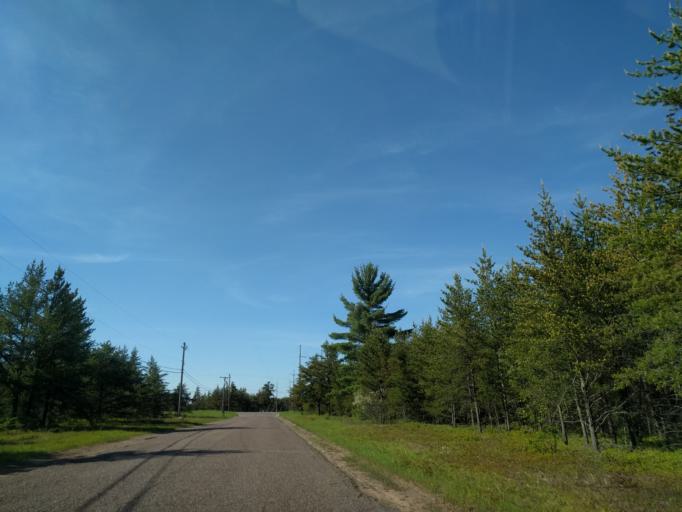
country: US
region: Michigan
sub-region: Marquette County
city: K. I. Sawyer Air Force Base
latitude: 46.2827
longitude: -87.3663
